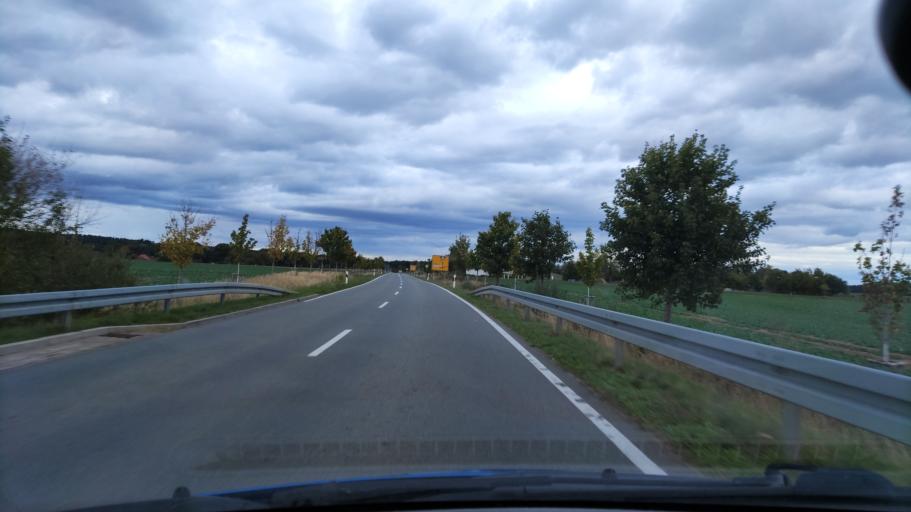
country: DE
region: Mecklenburg-Vorpommern
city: Lubtheen
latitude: 53.3638
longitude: 10.9644
